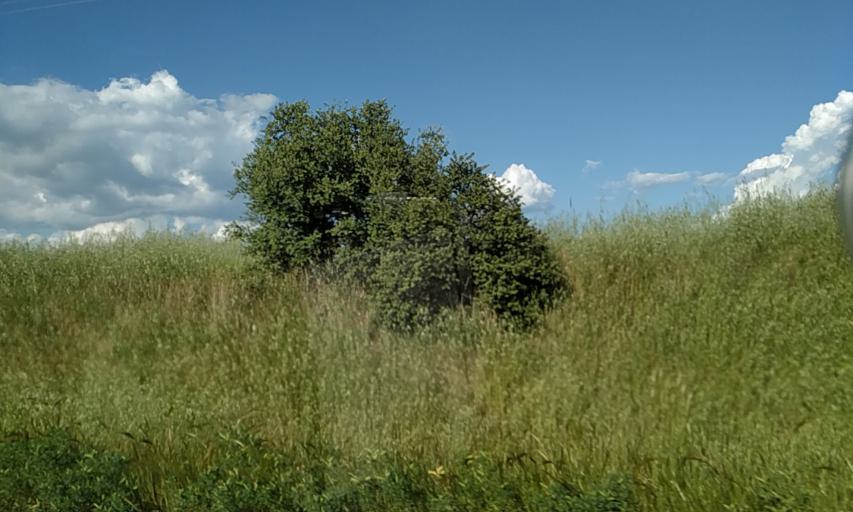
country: PT
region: Portalegre
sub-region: Portalegre
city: Urra
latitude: 39.1349
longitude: -7.4491
